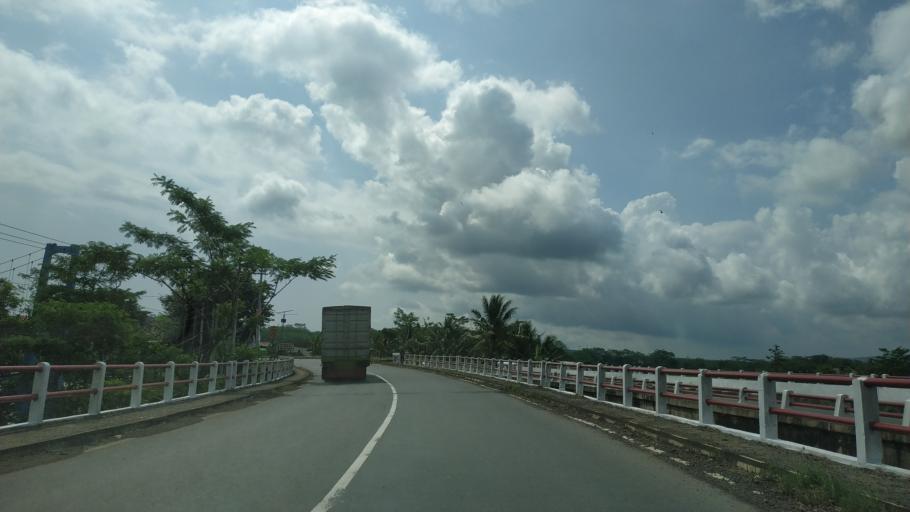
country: ID
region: Central Java
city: Pekalongan
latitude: -6.9526
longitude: 109.8070
